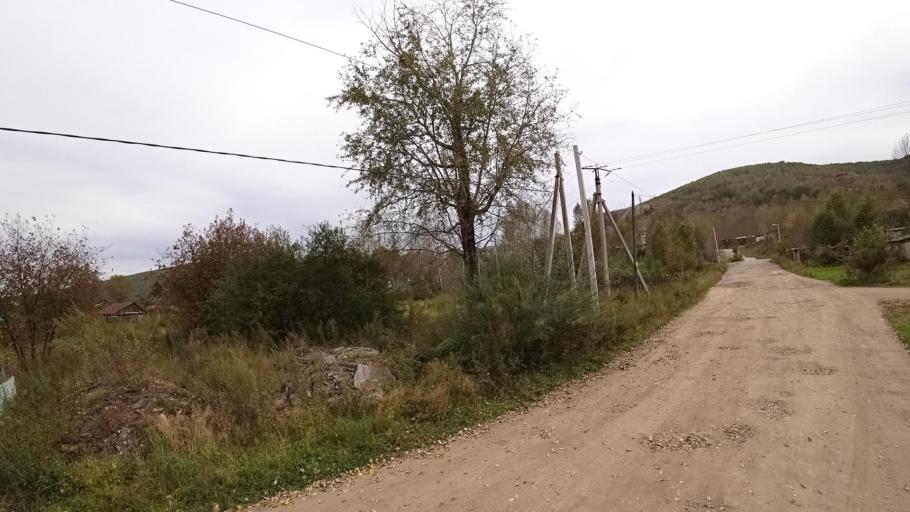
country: RU
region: Jewish Autonomous Oblast
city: Khingansk
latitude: 49.1279
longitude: 131.1875
